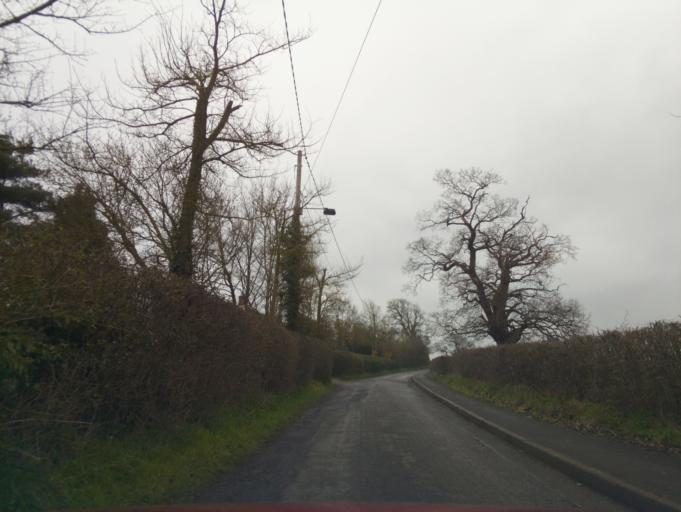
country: GB
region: England
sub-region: South Gloucestershire
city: Charfield
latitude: 51.6231
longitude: -2.3959
